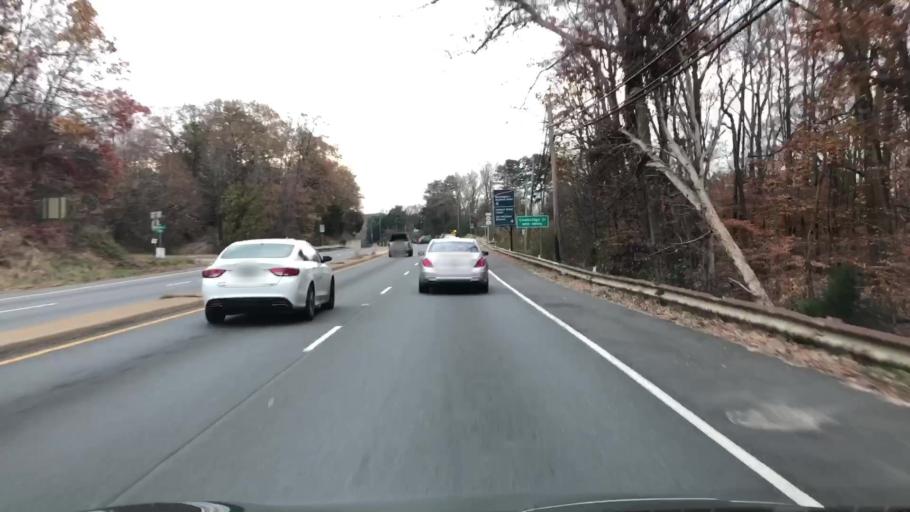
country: US
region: Virginia
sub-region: Stafford County
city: Falmouth
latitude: 38.3272
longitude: -77.4736
